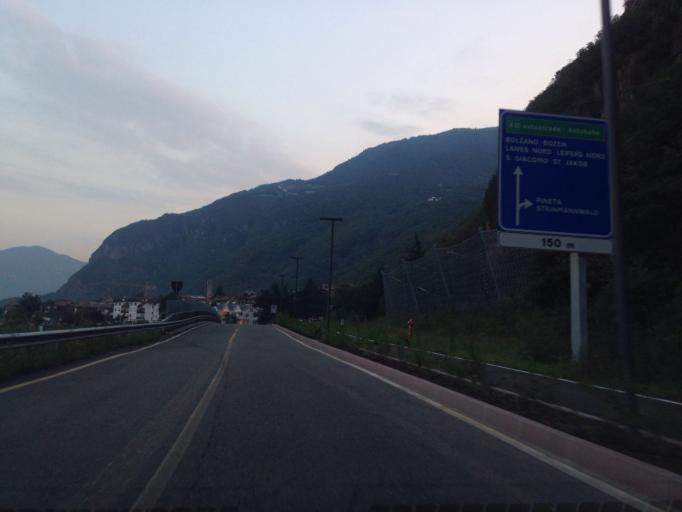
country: IT
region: Trentino-Alto Adige
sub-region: Bolzano
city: Pineta
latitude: 46.4333
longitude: 11.3468
